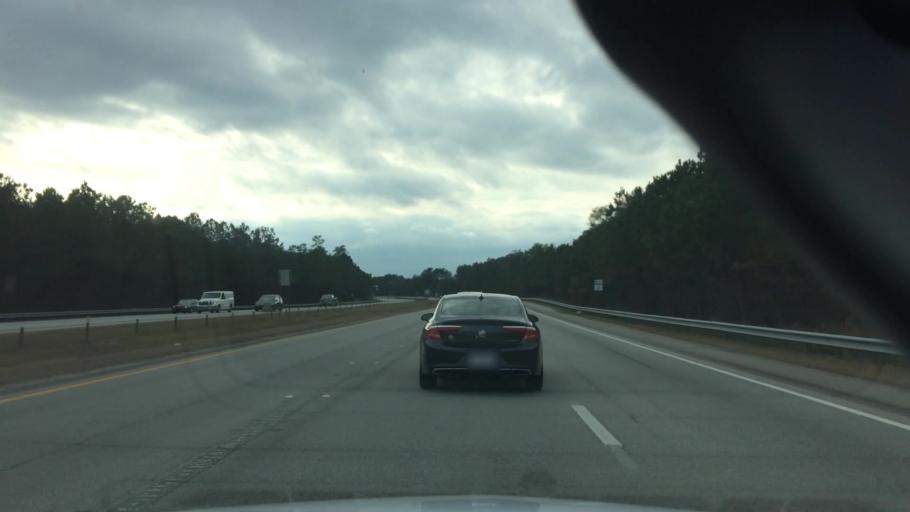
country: US
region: South Carolina
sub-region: Horry County
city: North Myrtle Beach
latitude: 33.8725
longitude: -78.6866
